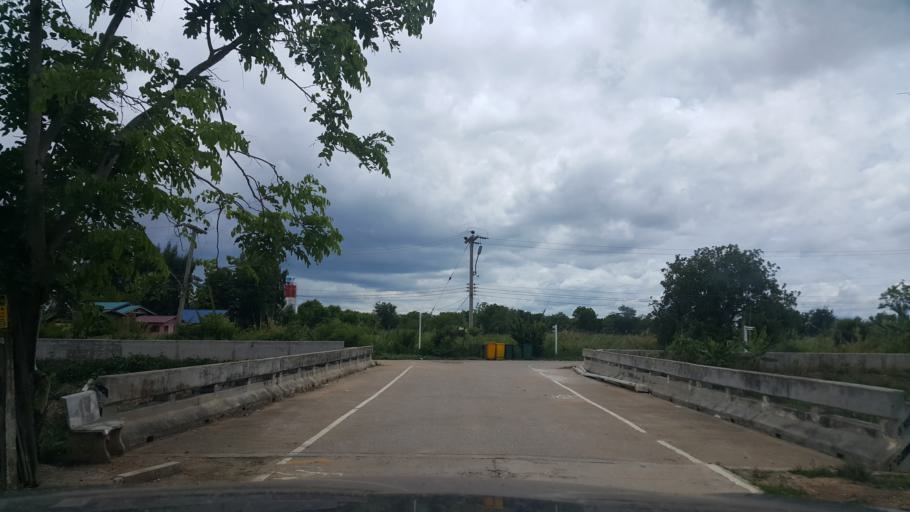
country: TH
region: Sukhothai
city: Sukhothai
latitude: 17.0162
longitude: 99.8084
